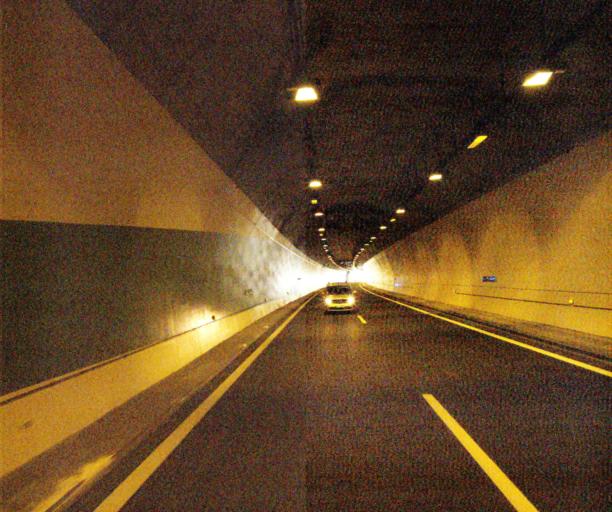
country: FR
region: Rhone-Alpes
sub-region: Departement de l'Isere
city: Vif
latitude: 45.0513
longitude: 5.6860
